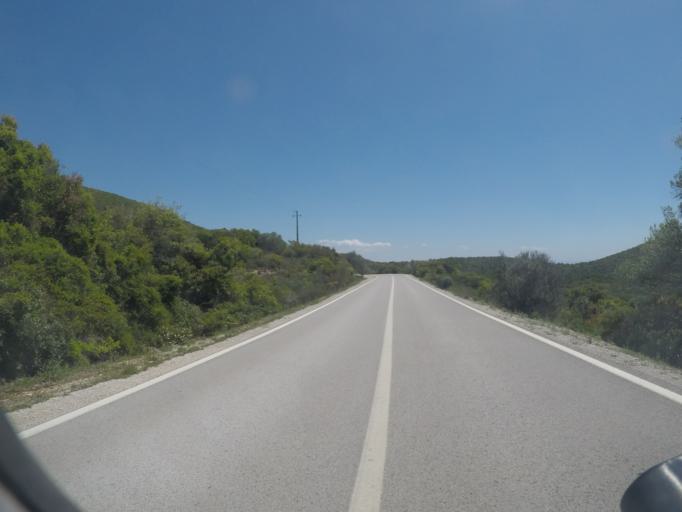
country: PT
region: Setubal
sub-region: Sesimbra
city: Sesimbra
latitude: 38.4607
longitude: -9.0242
